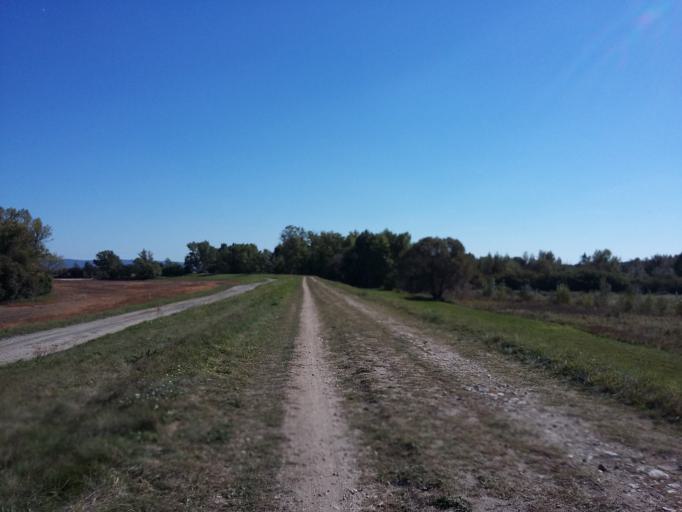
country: AT
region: Lower Austria
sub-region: Politischer Bezirk Ganserndorf
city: Marchegg
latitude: 48.3140
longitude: 16.9147
